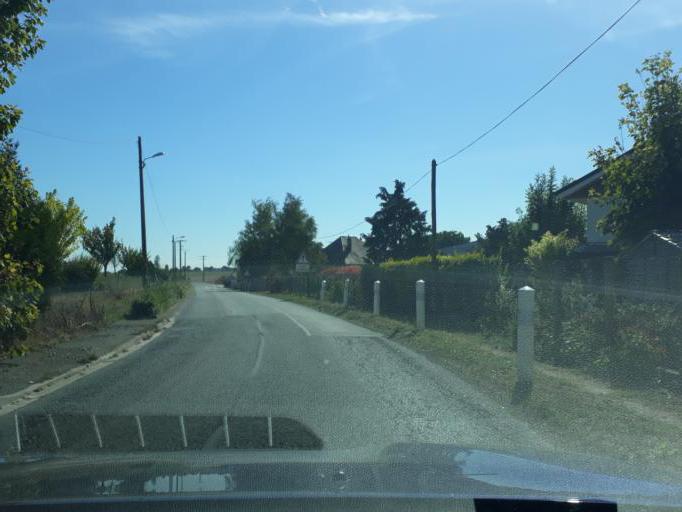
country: FR
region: Centre
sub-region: Departement du Loir-et-Cher
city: Ouzouer-le-Marche
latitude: 47.8857
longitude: 1.5494
